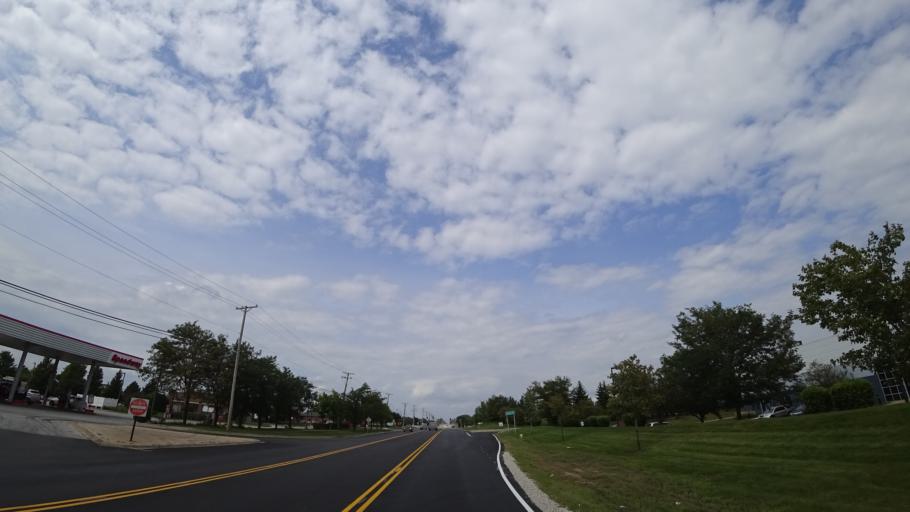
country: US
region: Illinois
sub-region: Cook County
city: Tinley Park
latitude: 41.5558
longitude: -87.8121
